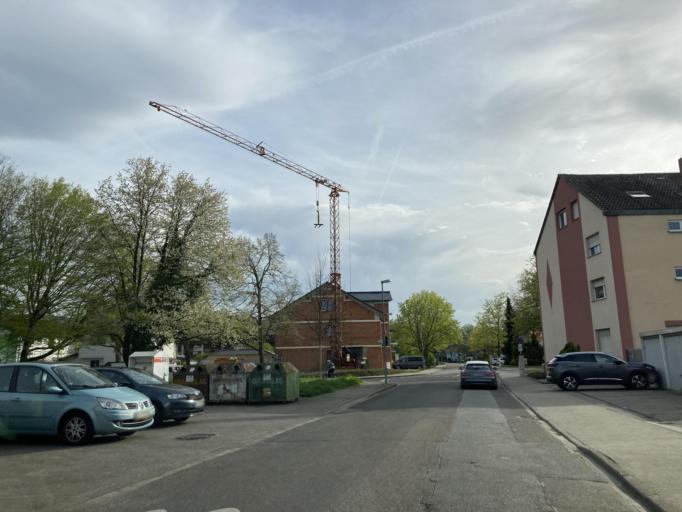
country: DE
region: Baden-Wuerttemberg
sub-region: Karlsruhe Region
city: Weingarten
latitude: 49.0917
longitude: 8.5497
